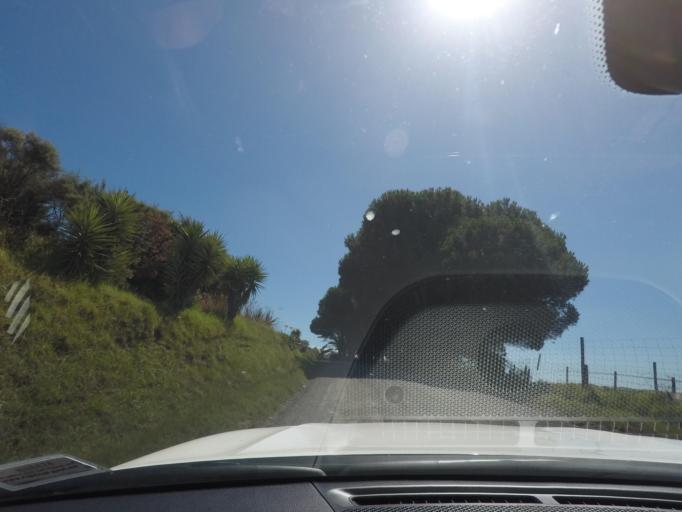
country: NZ
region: Auckland
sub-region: Auckland
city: Parakai
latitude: -36.5829
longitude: 174.2997
